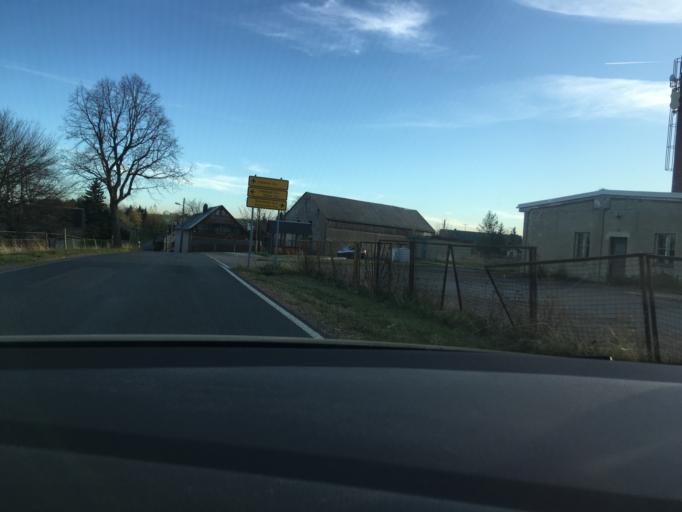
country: DE
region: Saxony
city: Barenstein
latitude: 50.8184
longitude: 13.8116
